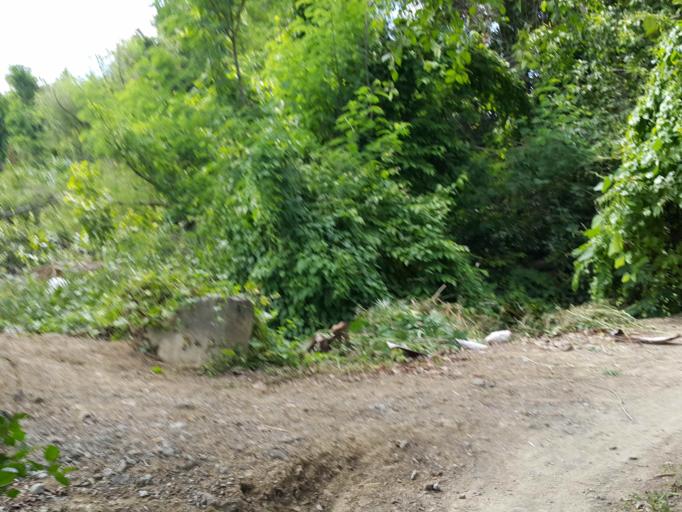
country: TH
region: Chiang Mai
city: San Kamphaeng
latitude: 18.7542
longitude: 99.0901
